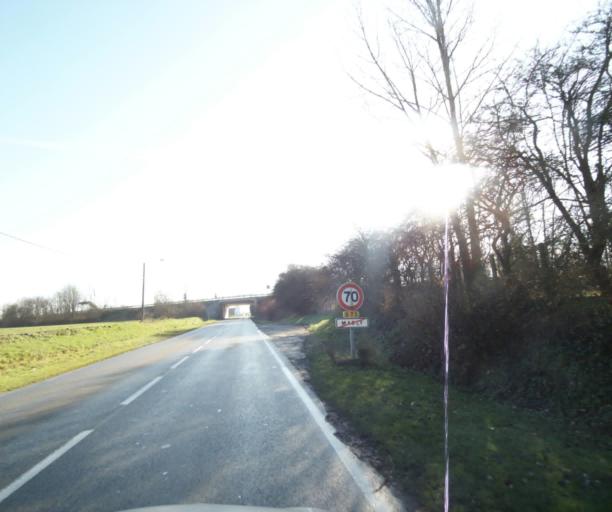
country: FR
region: Nord-Pas-de-Calais
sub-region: Departement du Nord
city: Marly
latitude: 50.3345
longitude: 3.5560
